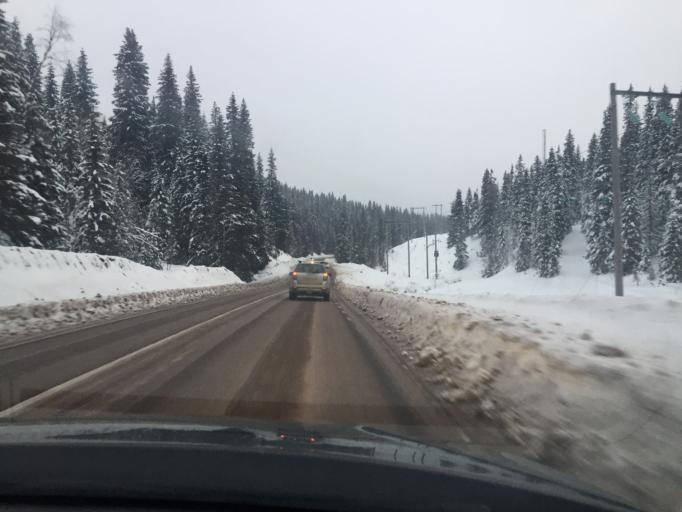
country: SE
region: Dalarna
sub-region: Malung-Saelens kommun
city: Malung
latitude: 61.1634
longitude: 13.1456
